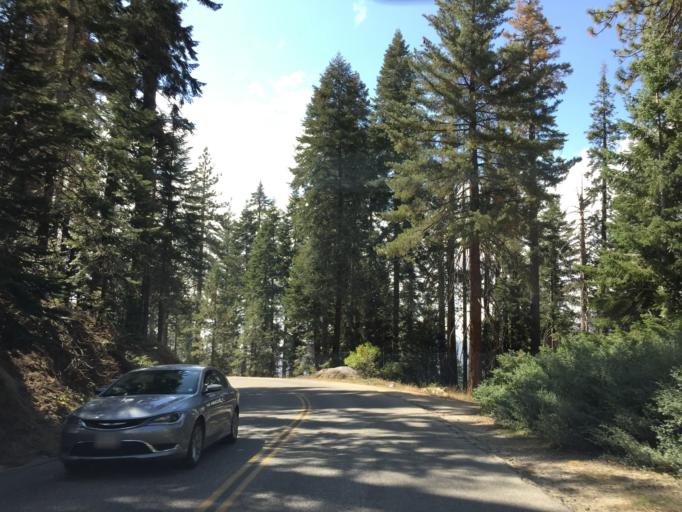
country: US
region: California
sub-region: Tulare County
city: Three Rivers
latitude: 36.5918
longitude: -118.7500
